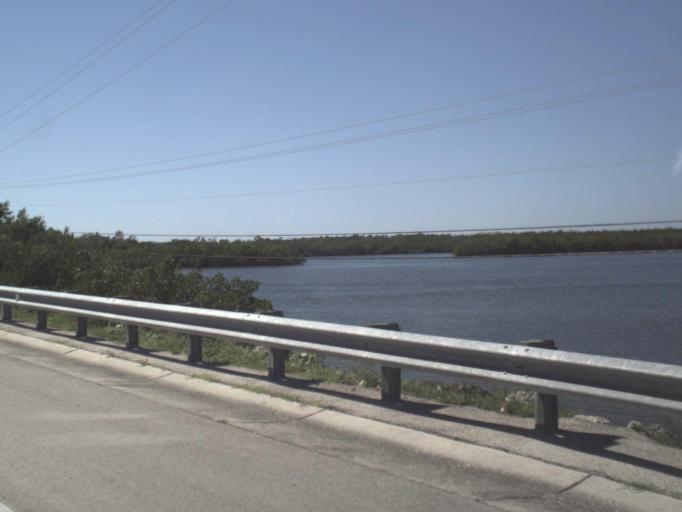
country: US
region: Florida
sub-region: Collier County
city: Marco
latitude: 25.9887
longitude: -81.7023
